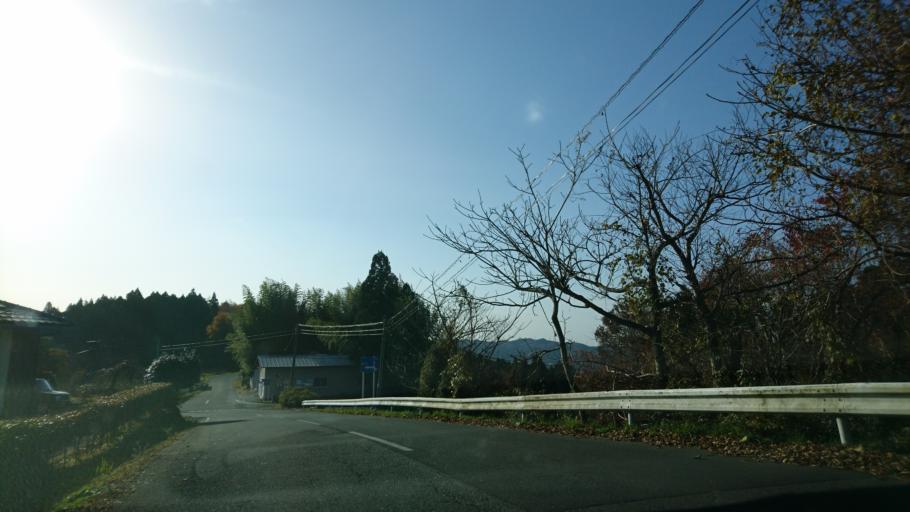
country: JP
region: Iwate
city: Ichinoseki
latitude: 38.8724
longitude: 141.3007
